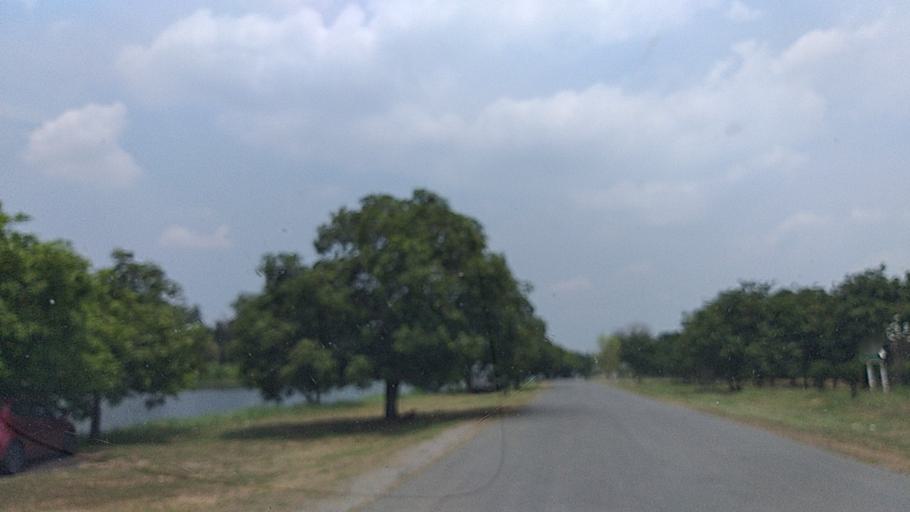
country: TH
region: Bangkok
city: Thawi Watthana
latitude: 13.7728
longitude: 100.3111
